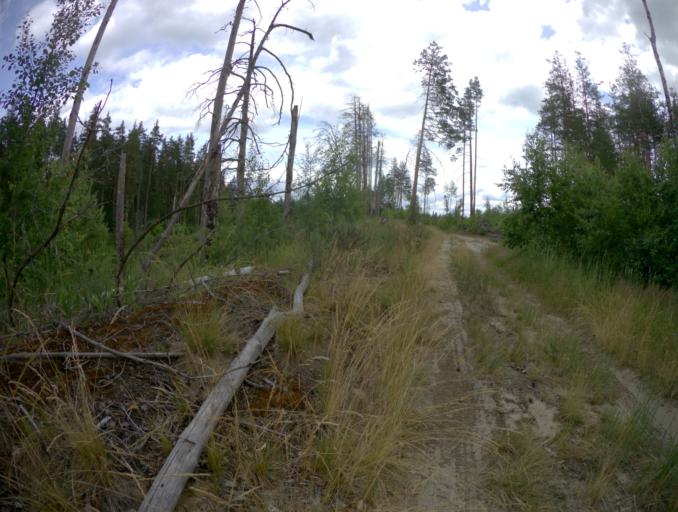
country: RU
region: Nizjnij Novgorod
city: Frolishchi
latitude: 56.4870
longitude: 42.5762
